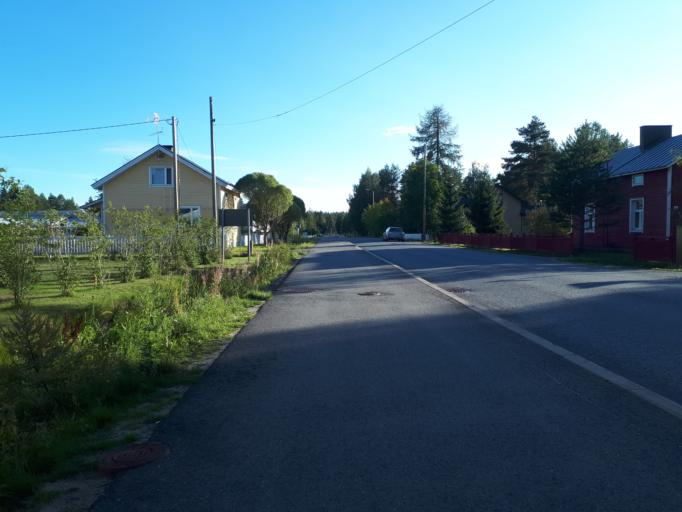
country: FI
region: Northern Ostrobothnia
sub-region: Oulunkaari
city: Ii
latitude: 65.3156
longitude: 25.3870
